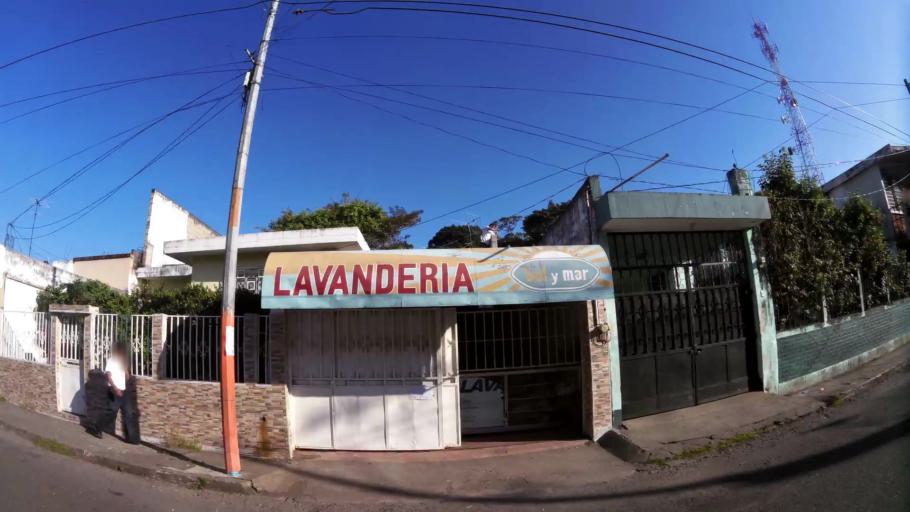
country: GT
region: Suchitepeque
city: Mazatenango
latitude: 14.5345
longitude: -91.5090
